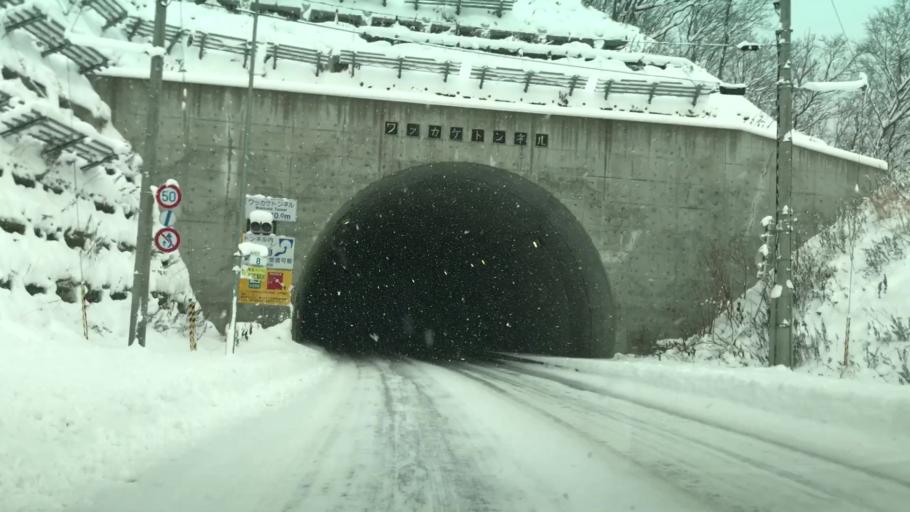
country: JP
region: Hokkaido
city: Yoichi
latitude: 43.2336
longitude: 140.7355
